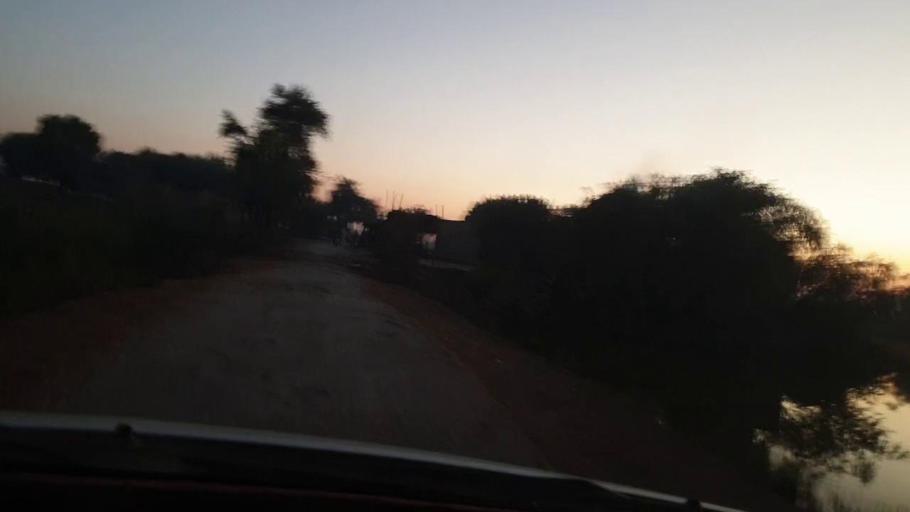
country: PK
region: Sindh
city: Khairpur Nathan Shah
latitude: 27.1386
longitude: 67.7178
